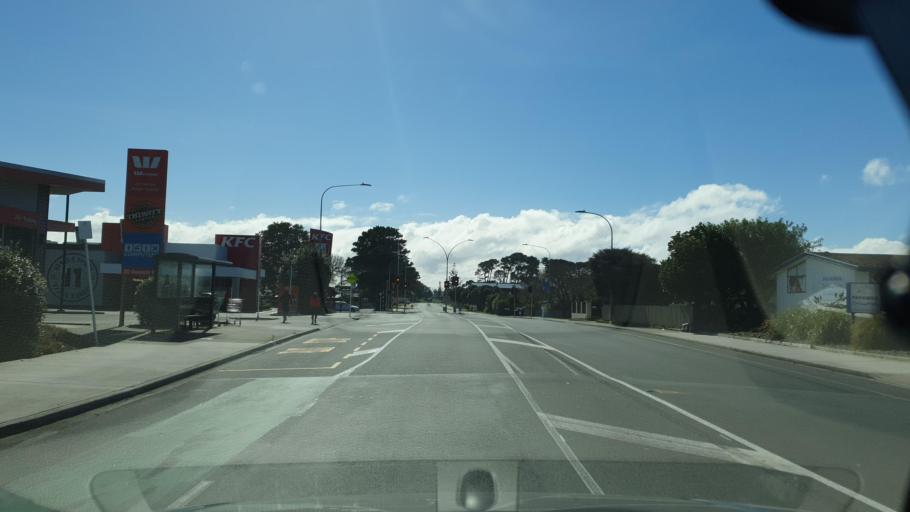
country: NZ
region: Bay of Plenty
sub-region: Tauranga City
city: Tauranga
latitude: -37.7017
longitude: 176.2847
